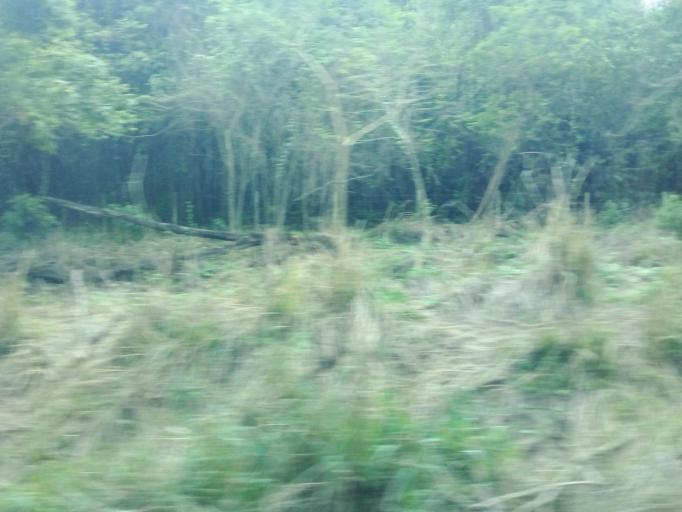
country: BR
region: Minas Gerais
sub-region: Ipaba
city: Ipaba
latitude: -19.4618
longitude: -42.4500
